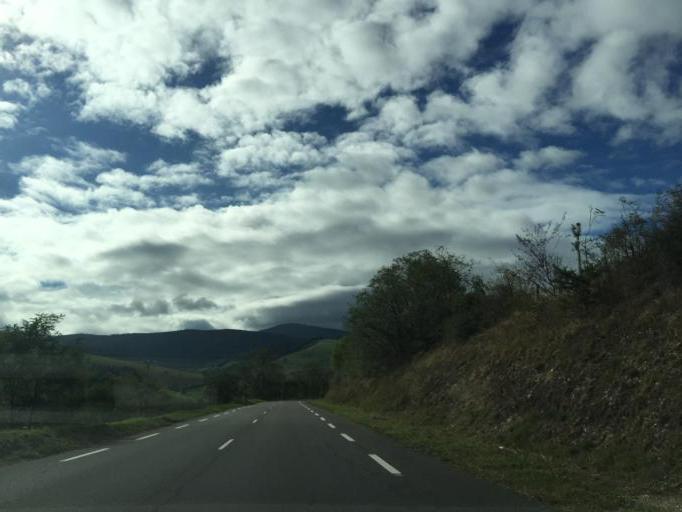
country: FR
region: Rhone-Alpes
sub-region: Departement de la Loire
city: Saint-Paul-en-Jarez
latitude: 45.4707
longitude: 4.5840
